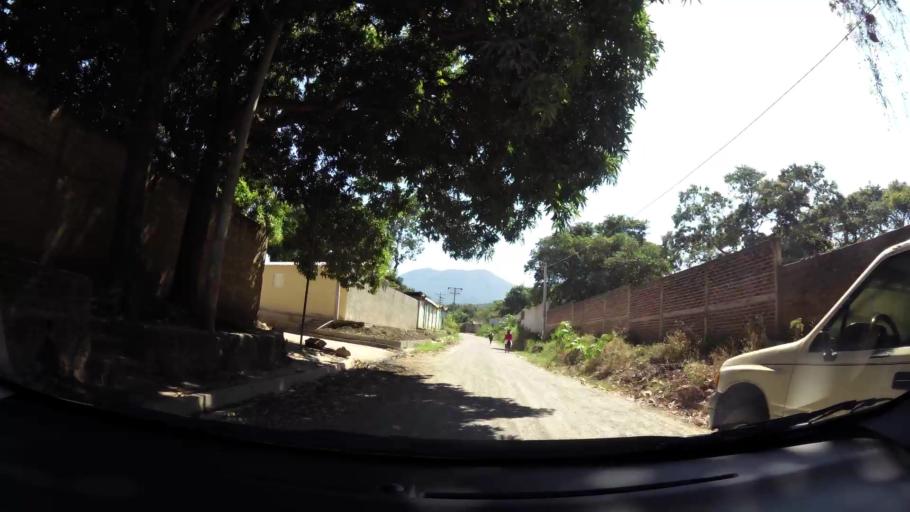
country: SV
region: Ahuachapan
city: Atiquizaya
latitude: 13.9691
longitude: -89.7574
